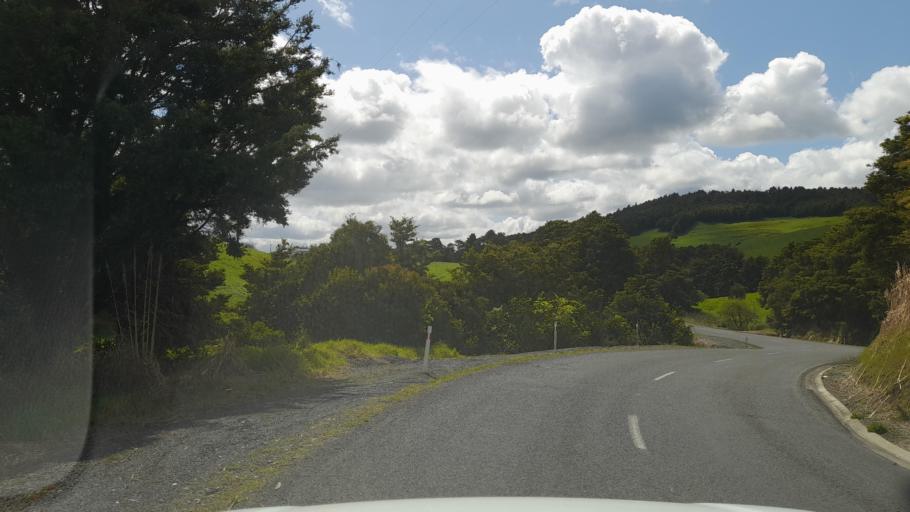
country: NZ
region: Northland
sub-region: Whangarei
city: Maungatapere
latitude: -35.7102
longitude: 174.0510
